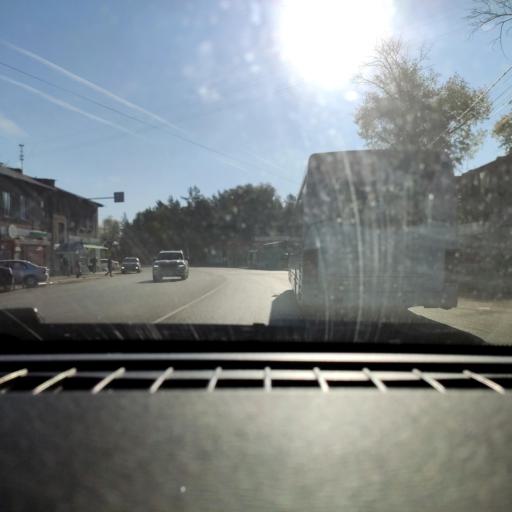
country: RU
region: Voronezj
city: Voronezh
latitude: 51.7243
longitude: 39.2630
